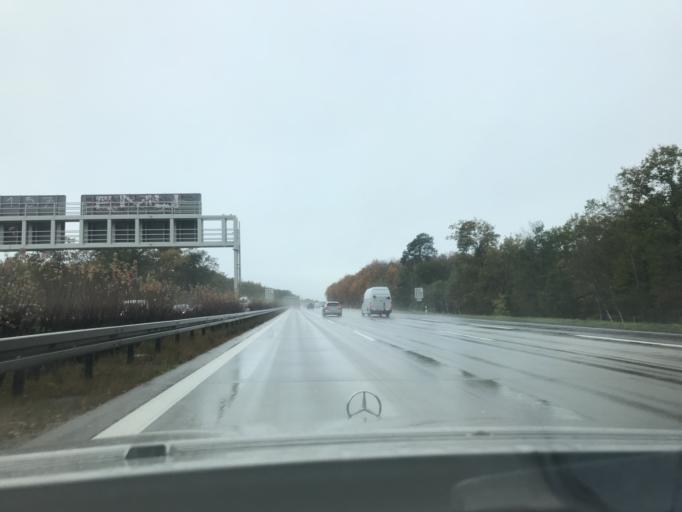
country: DE
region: Brandenburg
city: Mittenwalde
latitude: 52.3189
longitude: 13.5394
